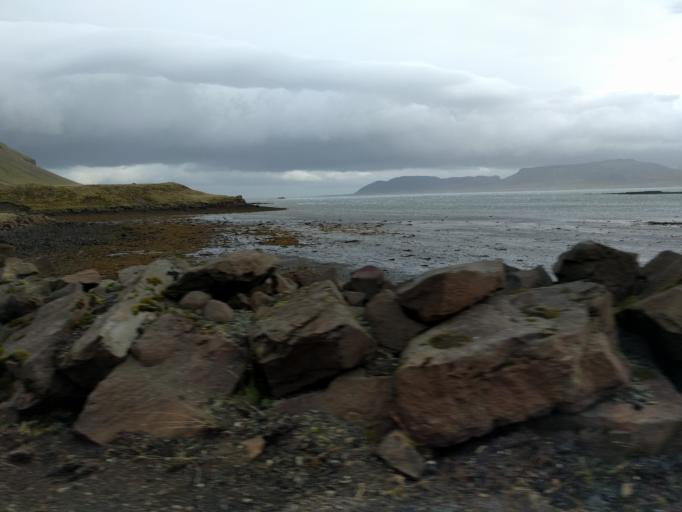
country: IS
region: West
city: Olafsvik
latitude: 64.9235
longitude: -23.2972
